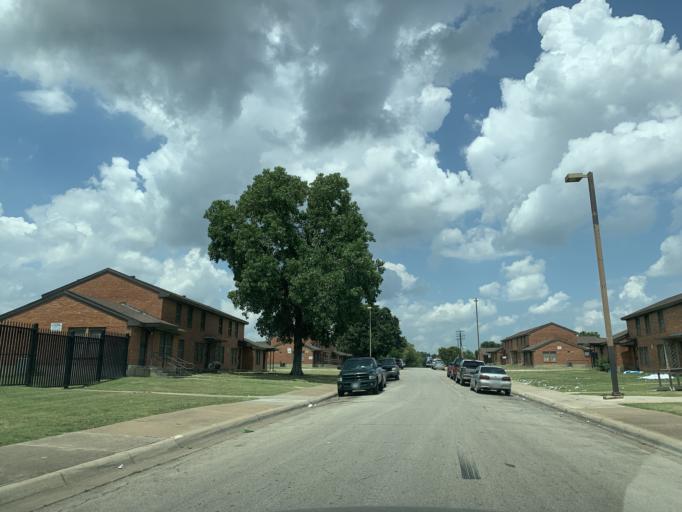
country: US
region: Texas
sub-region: Tarrant County
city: Forest Hill
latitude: 32.7287
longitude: -97.2479
